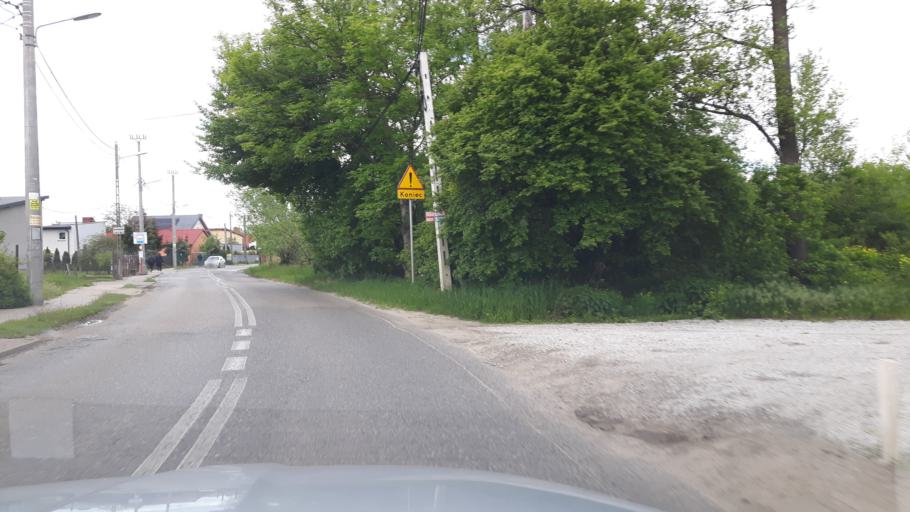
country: PL
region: Masovian Voivodeship
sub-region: Warszawa
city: Targowek
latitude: 52.3326
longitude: 21.0557
